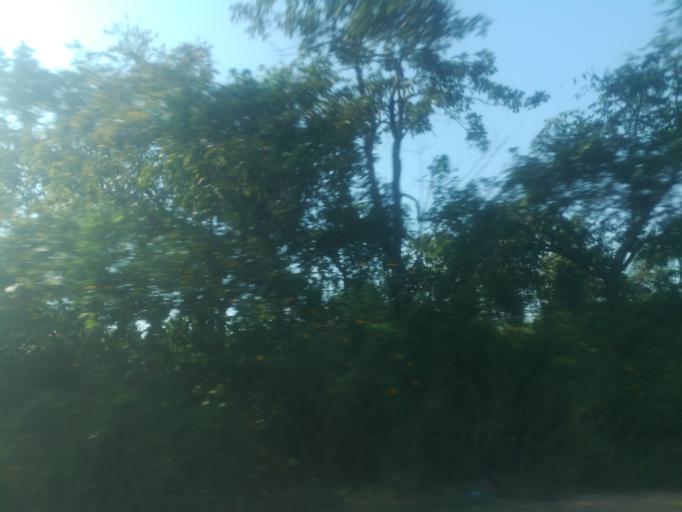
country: NG
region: Ogun
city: Abeokuta
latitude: 7.1430
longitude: 3.2544
